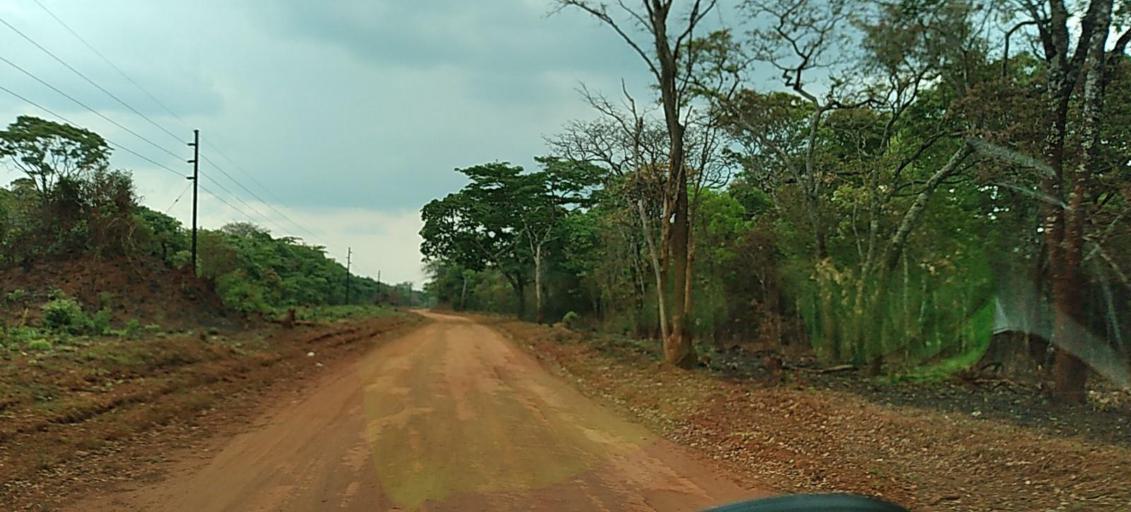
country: ZM
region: North-Western
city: Solwezi
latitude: -12.7811
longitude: 26.4855
